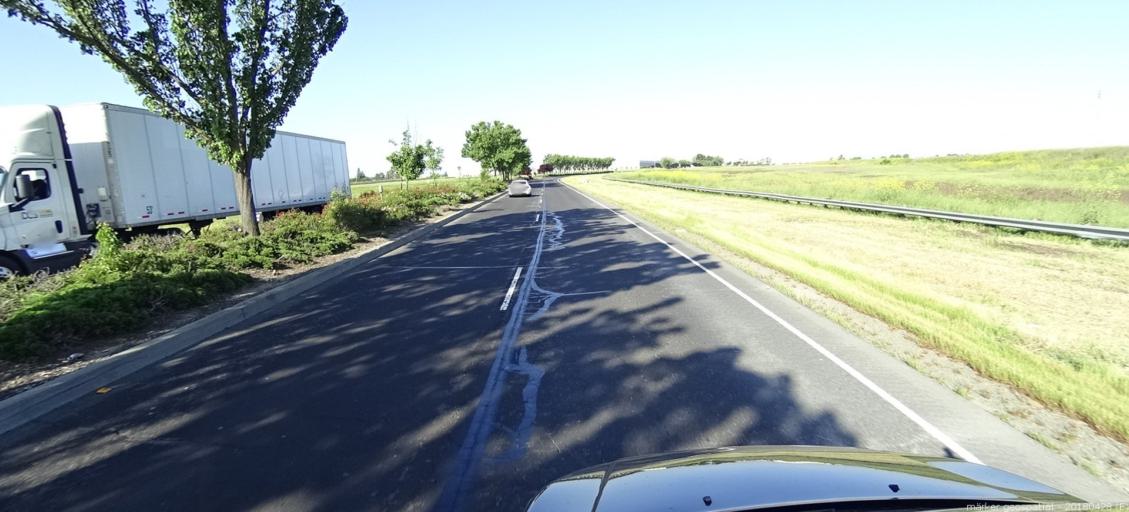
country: US
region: California
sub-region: Yolo County
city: West Sacramento
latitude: 38.5564
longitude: -121.5512
